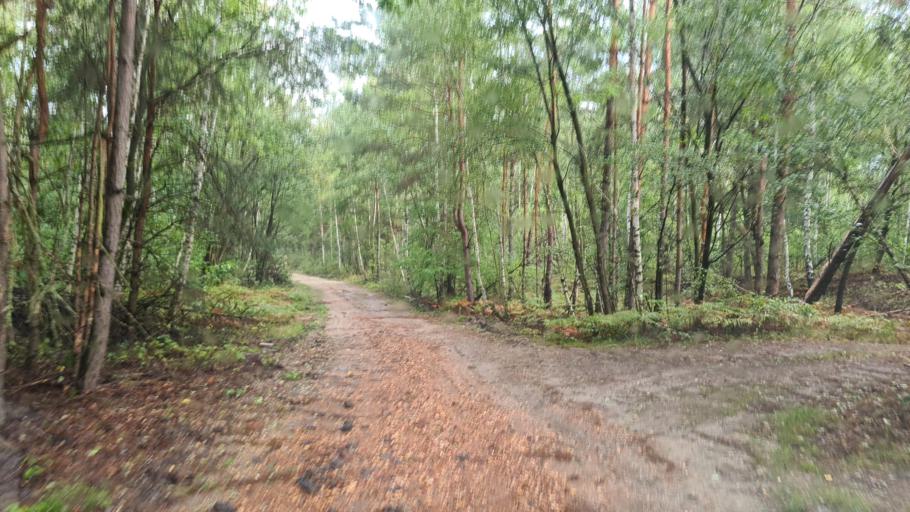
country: DE
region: Brandenburg
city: Sallgast
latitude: 51.5850
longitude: 13.8018
